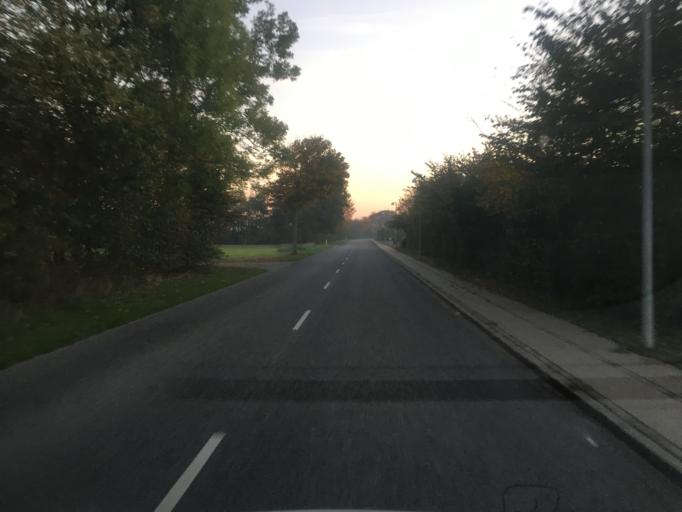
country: DE
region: Schleswig-Holstein
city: Bramstedtlund
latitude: 54.9462
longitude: 9.0922
